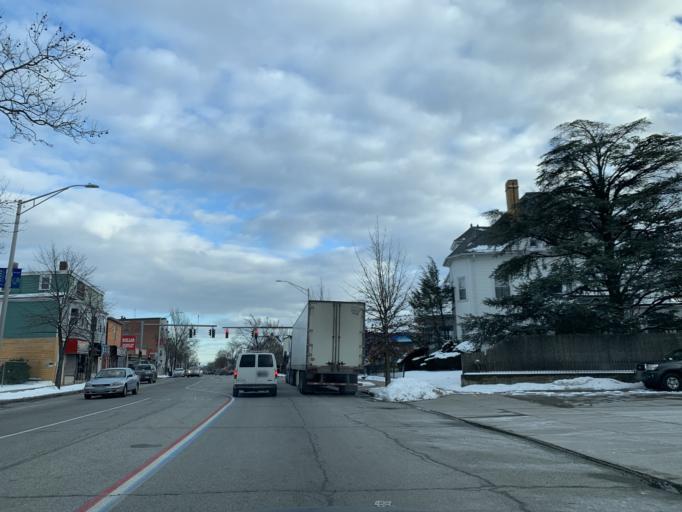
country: US
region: Rhode Island
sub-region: Providence County
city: Providence
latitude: 41.8010
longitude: -71.4180
